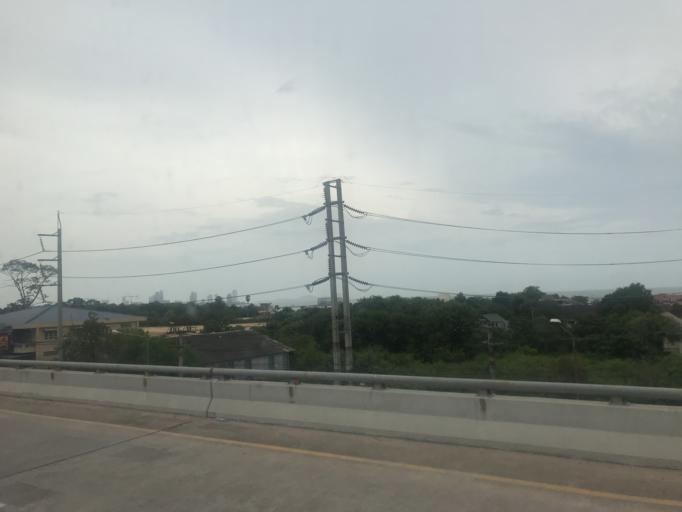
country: TH
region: Chon Buri
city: Bang Lamung
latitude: 13.0035
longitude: 100.9300
